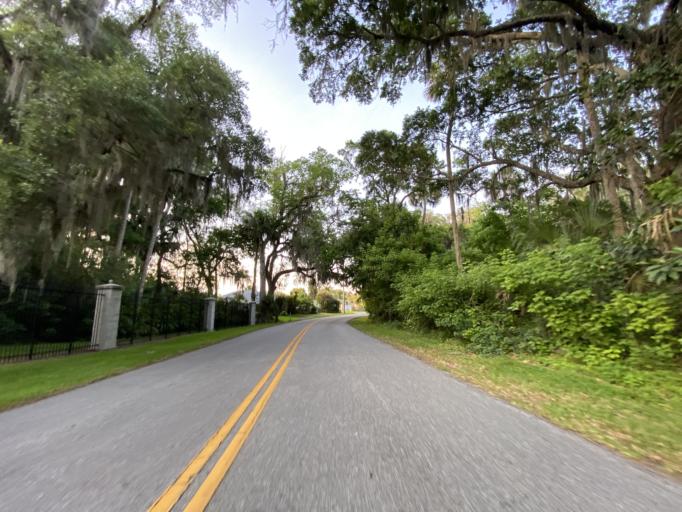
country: US
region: Florida
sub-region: Volusia County
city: Port Orange
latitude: 29.1413
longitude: -81.0055
